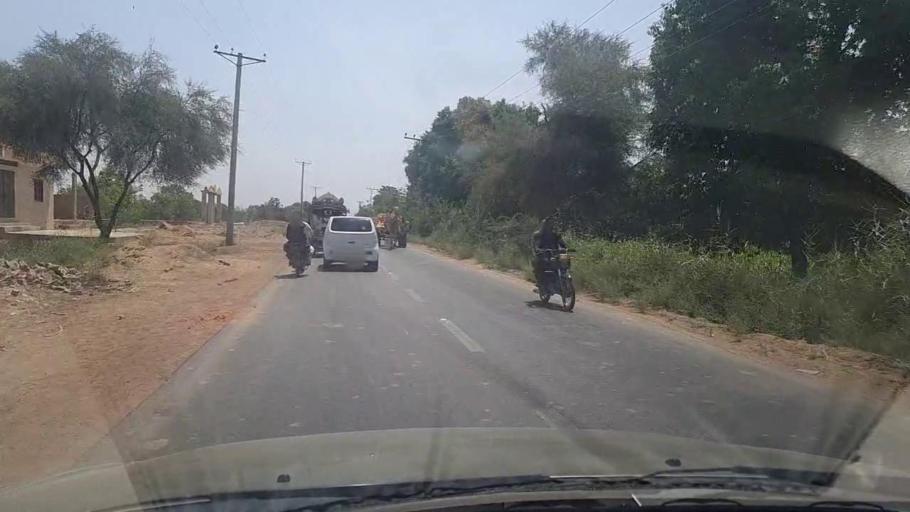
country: PK
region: Sindh
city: Hyderabad
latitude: 25.3909
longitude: 68.4083
